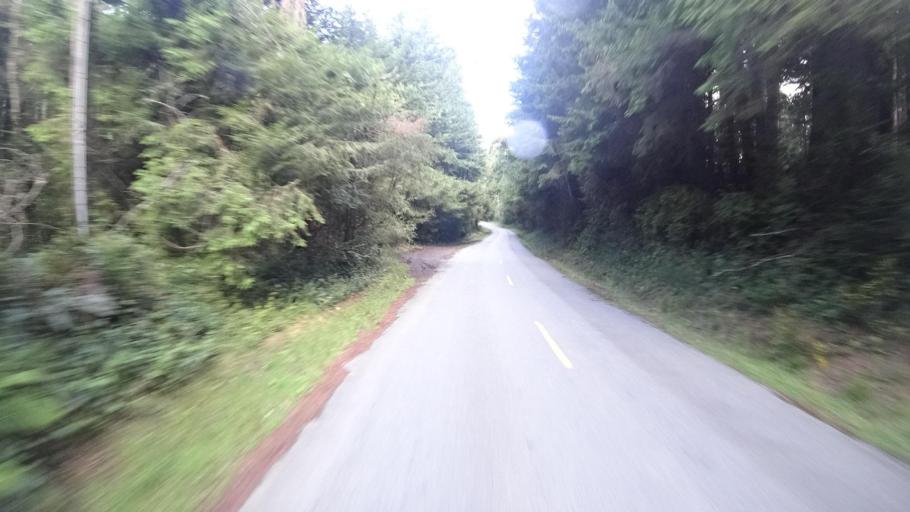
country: US
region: California
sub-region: Humboldt County
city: Westhaven-Moonstone
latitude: 41.0609
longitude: -124.1351
